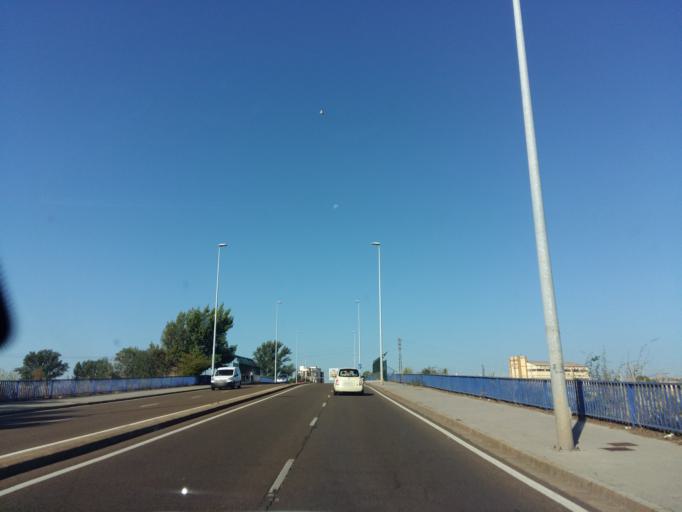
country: ES
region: Castille and Leon
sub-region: Provincia de Leon
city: Leon
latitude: 42.5857
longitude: -5.5783
